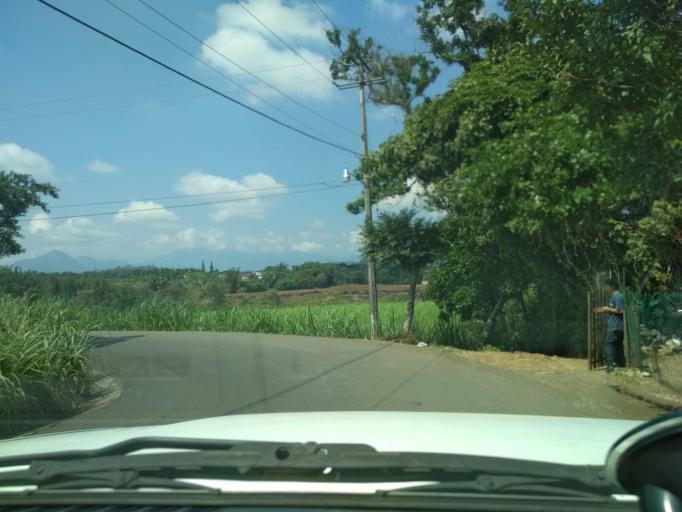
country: MX
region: Veracruz
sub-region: Fortin
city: Cordoba (Santa Leticia)
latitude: 18.9131
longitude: -96.9724
